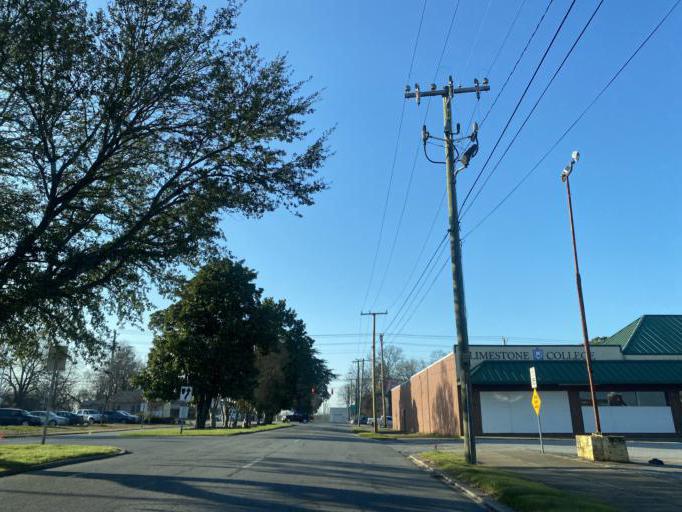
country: US
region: South Carolina
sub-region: Cherokee County
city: Gaffney
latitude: 35.0733
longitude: -81.6514
